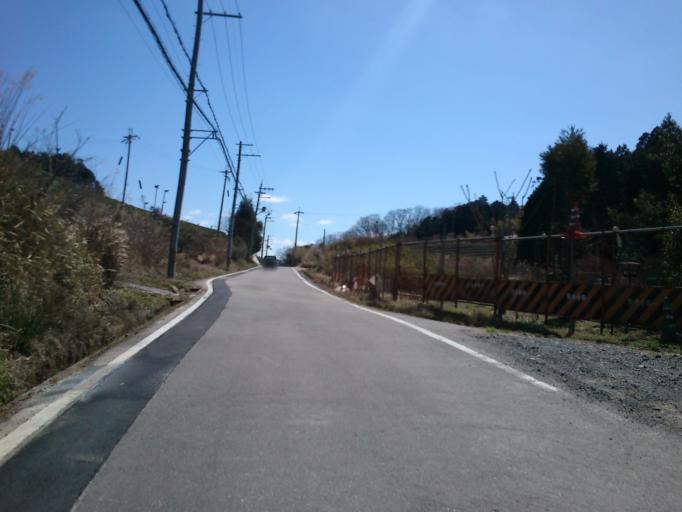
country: JP
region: Nara
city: Nara-shi
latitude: 34.7754
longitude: 135.9086
